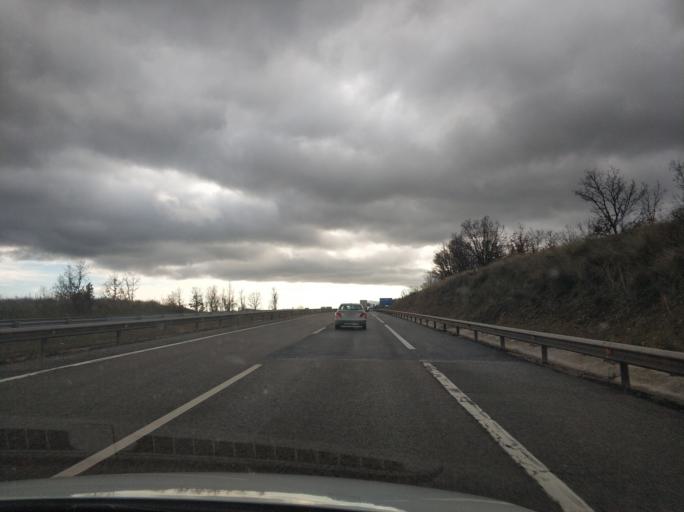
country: ES
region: Madrid
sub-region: Provincia de Madrid
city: Horcajo de la Sierra
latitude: 41.0730
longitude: -3.6052
